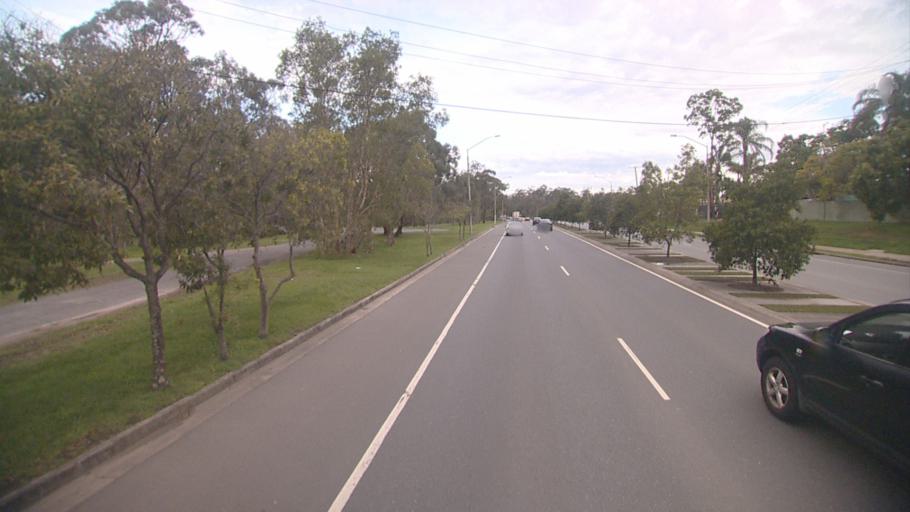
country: AU
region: Queensland
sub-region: Logan
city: Woodridge
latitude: -27.6651
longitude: 153.0648
